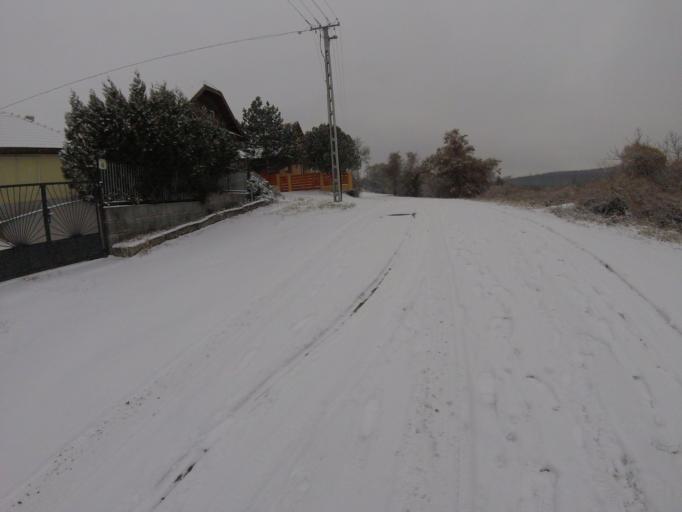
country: HU
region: Fejer
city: Pakozd
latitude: 47.2193
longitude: 18.5400
